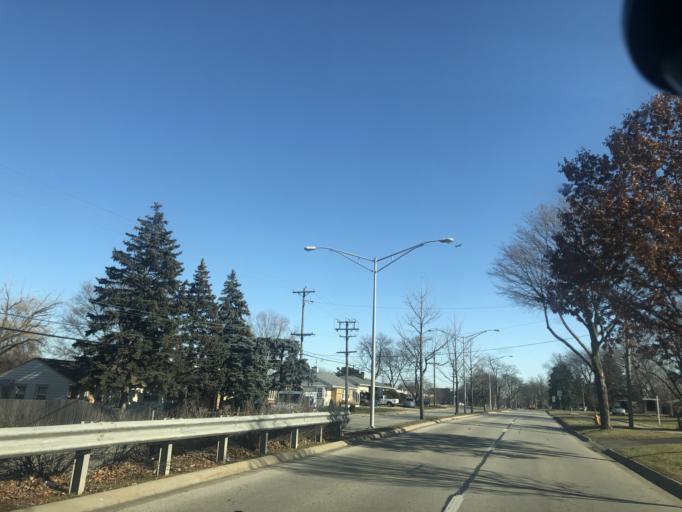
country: US
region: Illinois
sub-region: DuPage County
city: Addison
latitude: 41.9316
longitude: -88.0002
